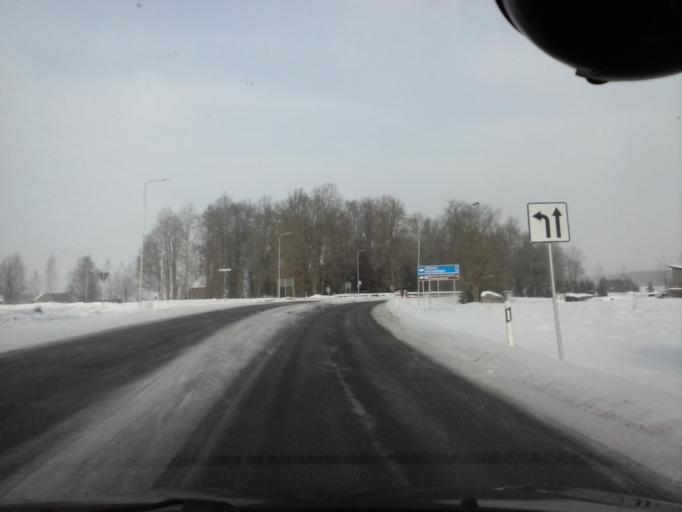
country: EE
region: Viljandimaa
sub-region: Abja vald
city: Abja-Paluoja
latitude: 58.3306
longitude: 25.3128
